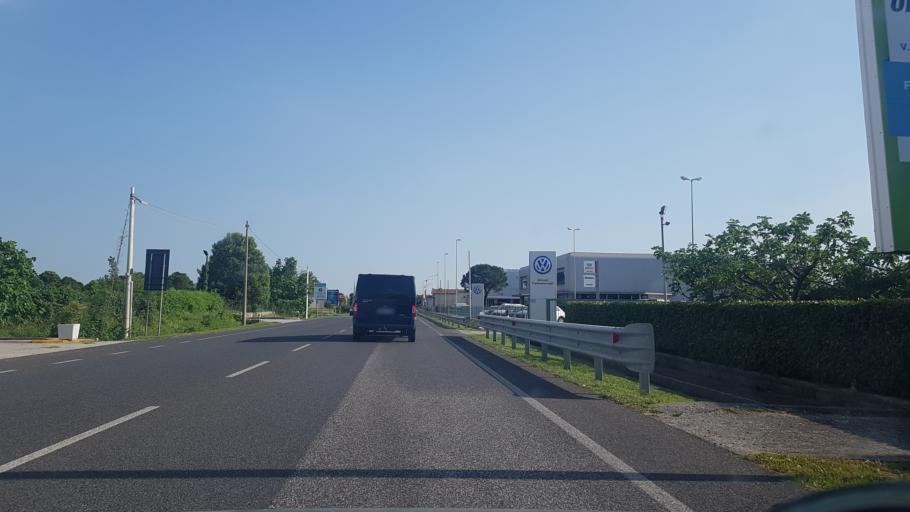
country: IT
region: Friuli Venezia Giulia
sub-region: Provincia di Udine
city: Gemona
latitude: 46.2717
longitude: 13.1079
